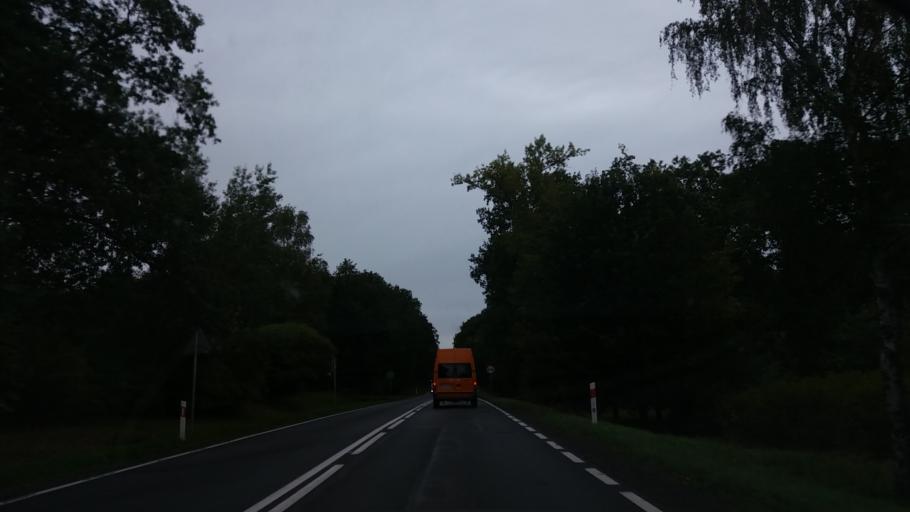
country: PL
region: Lower Silesian Voivodeship
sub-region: Powiat legnicki
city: Prochowice
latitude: 51.2946
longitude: 16.3447
